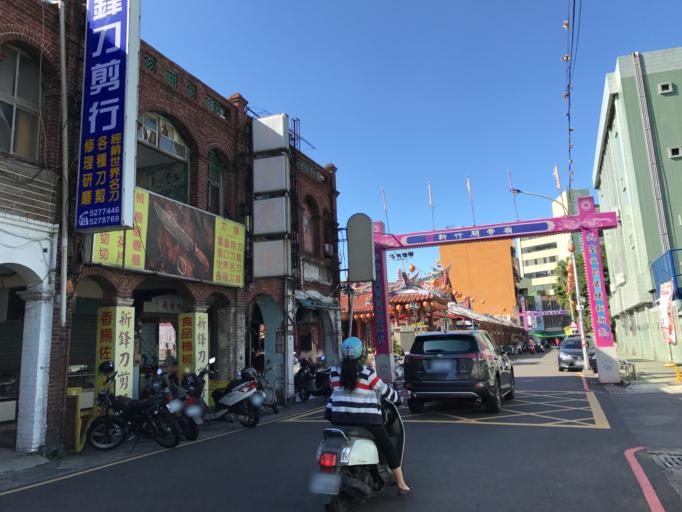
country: TW
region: Taiwan
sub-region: Hsinchu
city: Hsinchu
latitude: 24.8024
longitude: 120.9669
